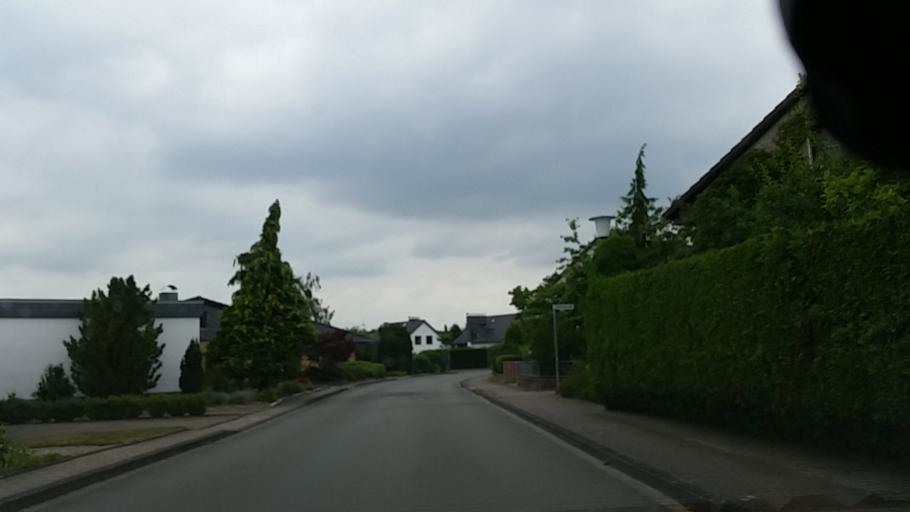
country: DE
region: Lower Saxony
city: Wolfsburg
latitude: 52.4512
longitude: 10.7865
